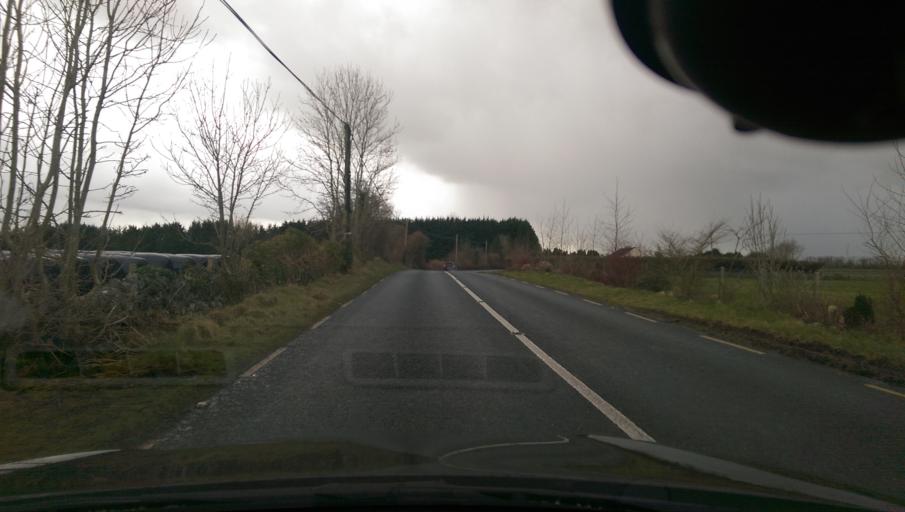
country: IE
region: Connaught
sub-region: County Galway
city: Athenry
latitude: 53.3549
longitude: -8.7415
